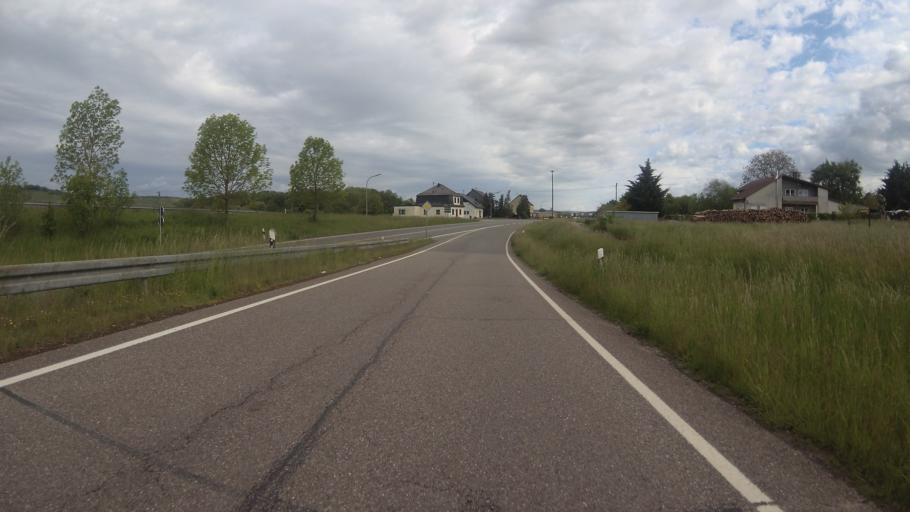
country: LU
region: Grevenmacher
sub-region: Canton de Remich
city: Remich
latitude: 49.5096
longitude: 6.3726
